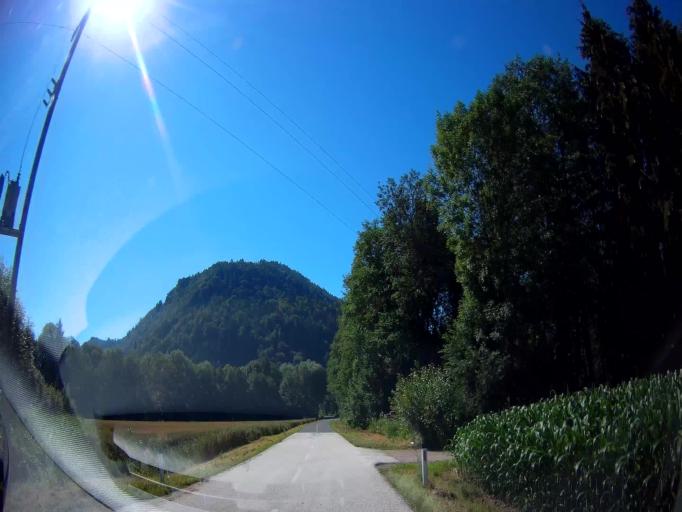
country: AT
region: Carinthia
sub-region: Politischer Bezirk Klagenfurt Land
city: Grafenstein
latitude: 46.6078
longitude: 14.4404
